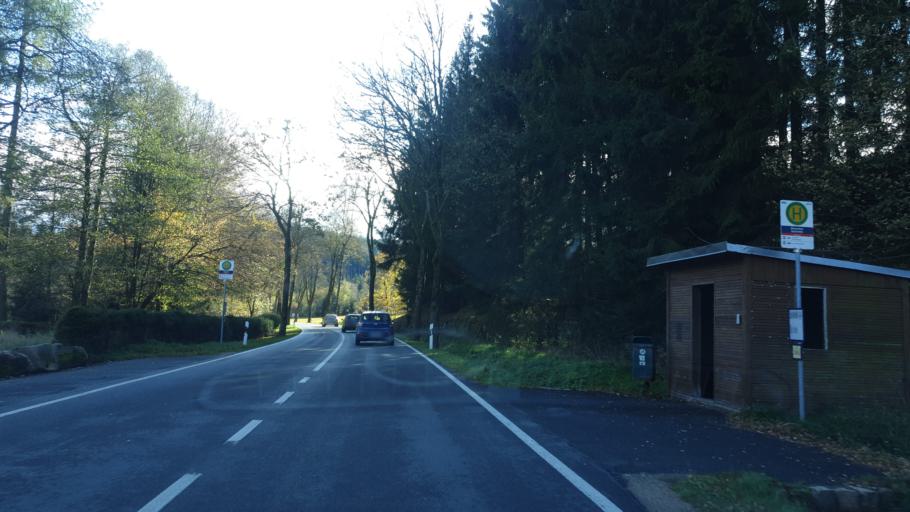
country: DE
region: Saxony
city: Sosa
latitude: 50.5205
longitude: 12.6344
